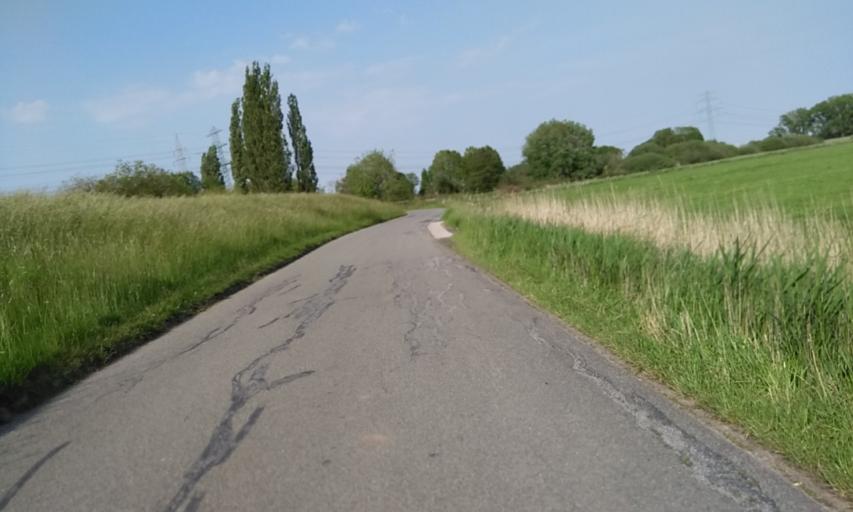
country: DE
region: Lower Saxony
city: Buxtehude
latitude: 53.4888
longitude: 9.7131
